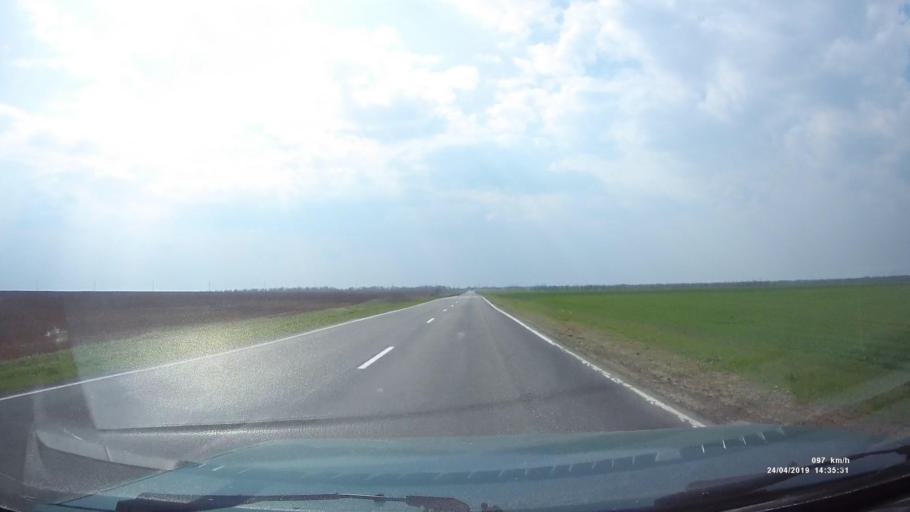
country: RU
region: Rostov
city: Remontnoye
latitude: 46.3739
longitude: 43.9091
